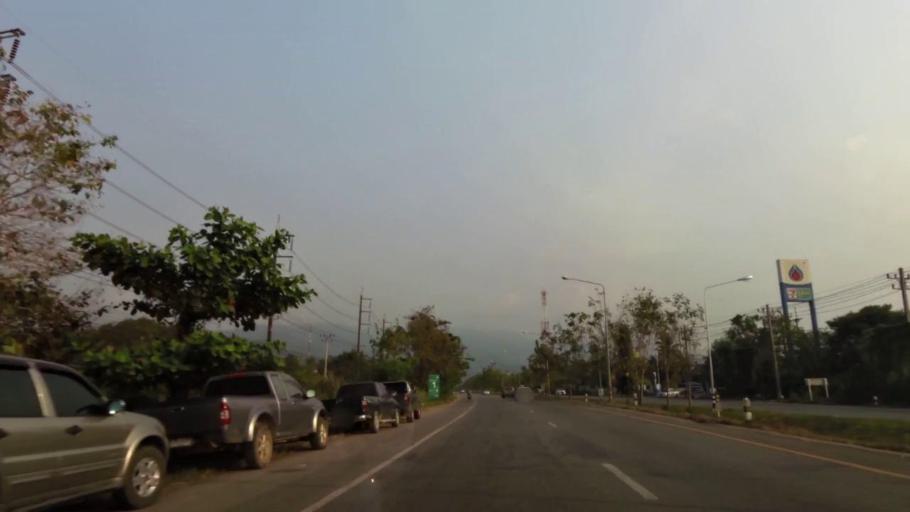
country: TH
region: Chanthaburi
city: Chanthaburi
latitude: 12.5965
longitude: 102.1425
